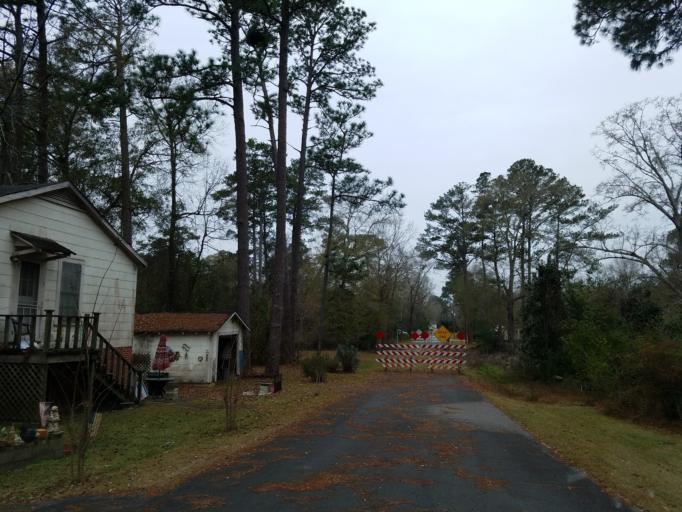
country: US
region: Mississippi
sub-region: Forrest County
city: Hattiesburg
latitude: 31.3185
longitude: -89.3186
